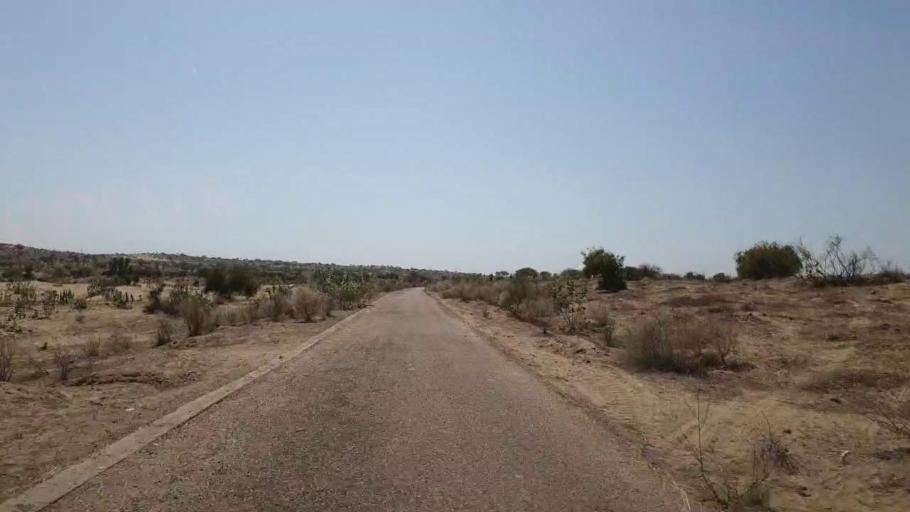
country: PK
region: Sindh
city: Umarkot
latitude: 25.1822
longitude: 69.8795
